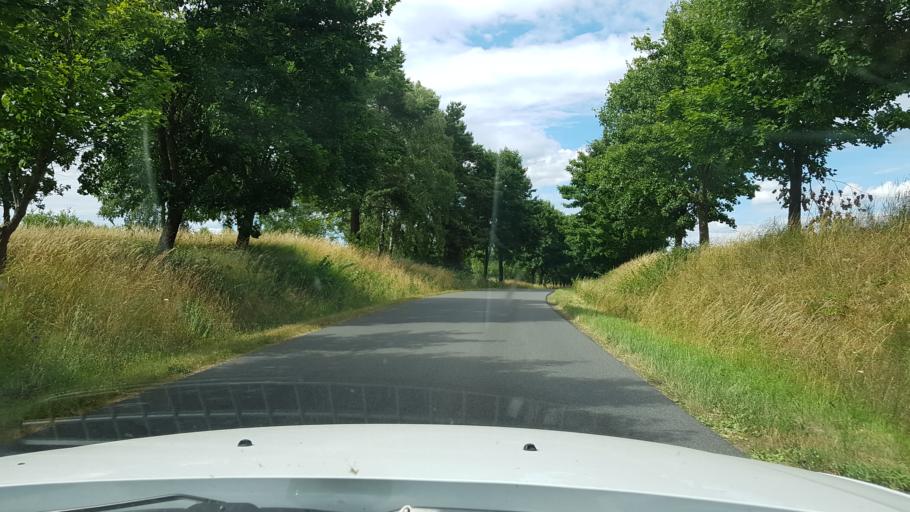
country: PL
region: West Pomeranian Voivodeship
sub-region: Powiat drawski
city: Kalisz Pomorski
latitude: 53.3089
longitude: 15.9192
